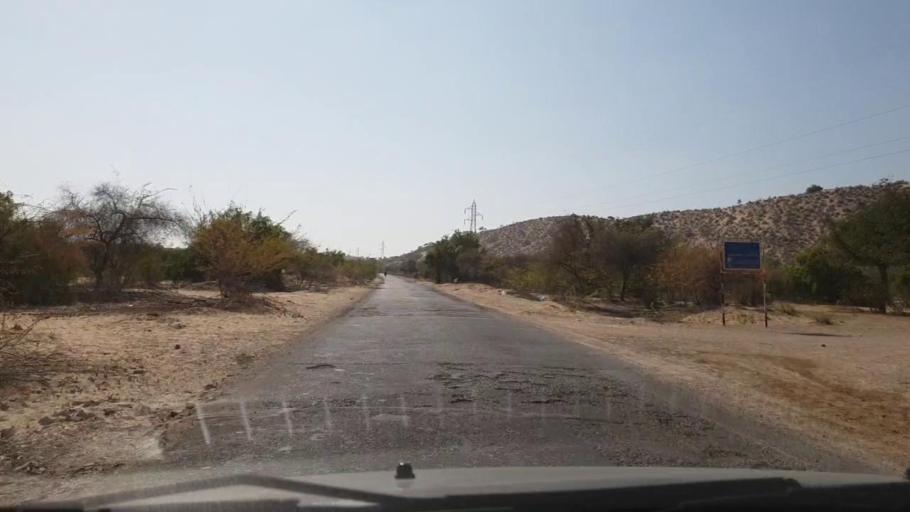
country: PK
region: Sindh
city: Mithi
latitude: 24.6436
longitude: 69.7464
